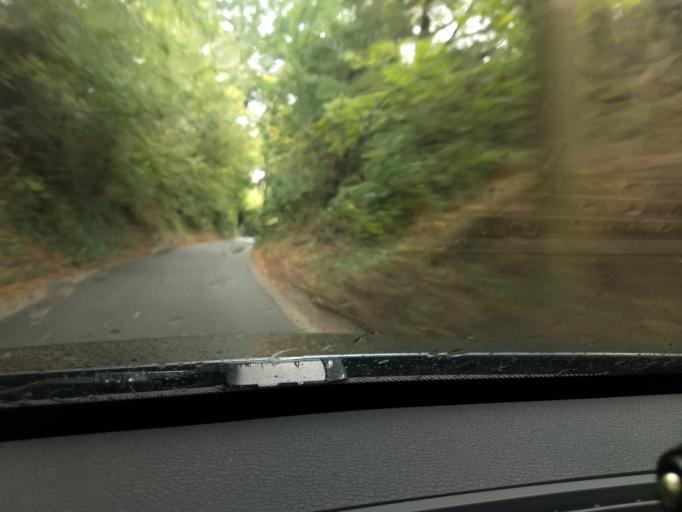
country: BE
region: Wallonia
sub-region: Province du Brabant Wallon
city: Braine-l'Alleud
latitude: 50.6711
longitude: 4.3729
